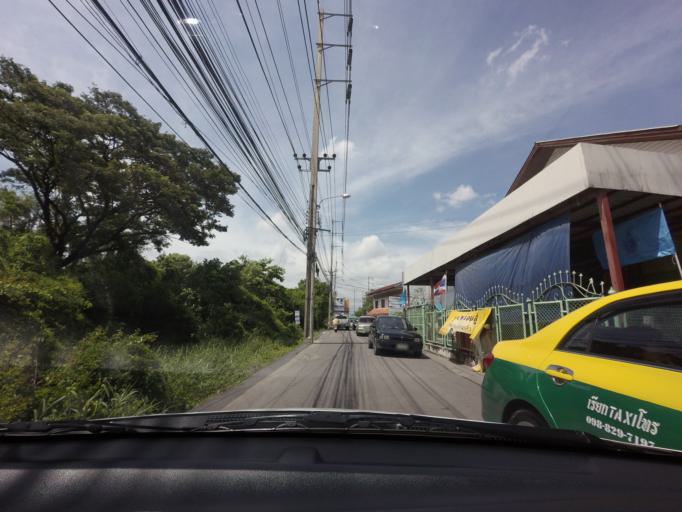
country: TH
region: Bangkok
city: Bang Na
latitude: 13.6143
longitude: 100.6738
